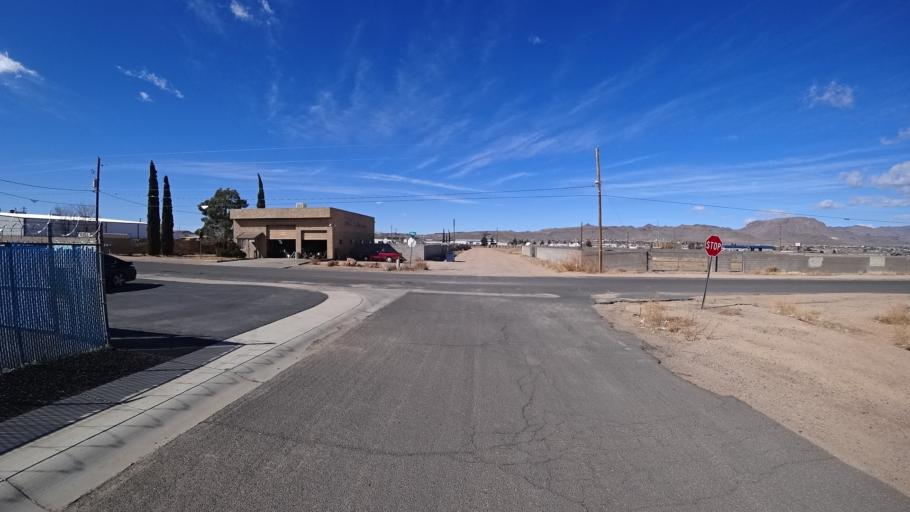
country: US
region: Arizona
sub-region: Mohave County
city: New Kingman-Butler
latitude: 35.2235
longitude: -114.0091
